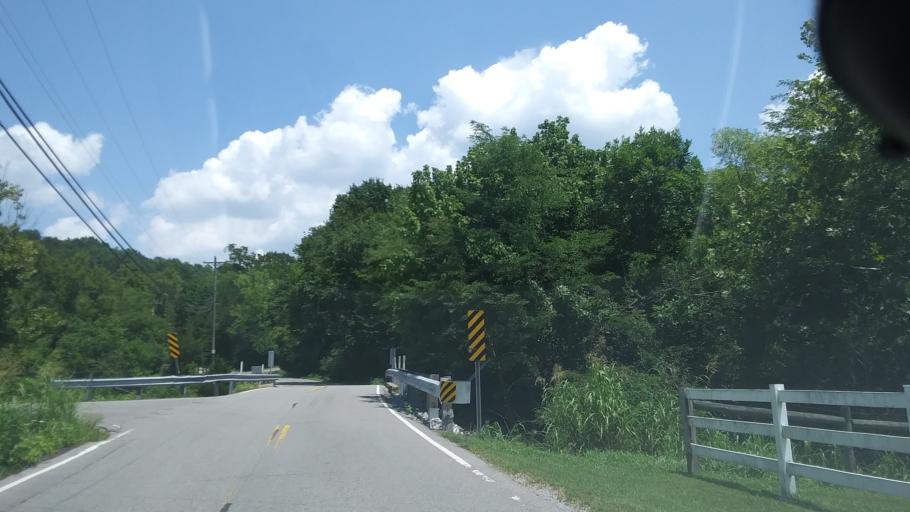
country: US
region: Tennessee
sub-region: Davidson County
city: Belle Meade
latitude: 36.1214
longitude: -86.9331
